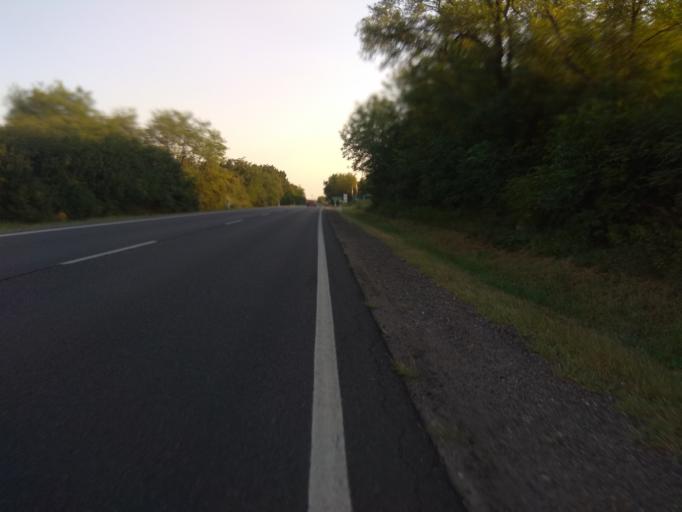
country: HU
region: Borsod-Abauj-Zemplen
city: Emod
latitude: 47.9548
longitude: 20.8340
